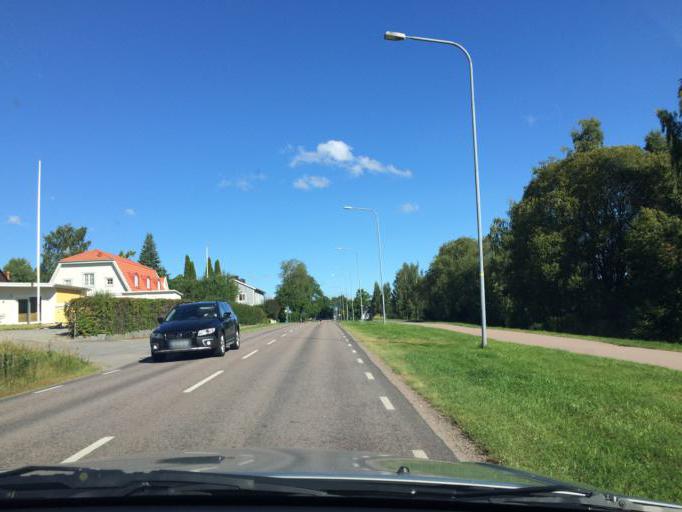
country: SE
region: Vaestmanland
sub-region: Vasteras
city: Vasteras
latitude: 59.5952
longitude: 16.5969
